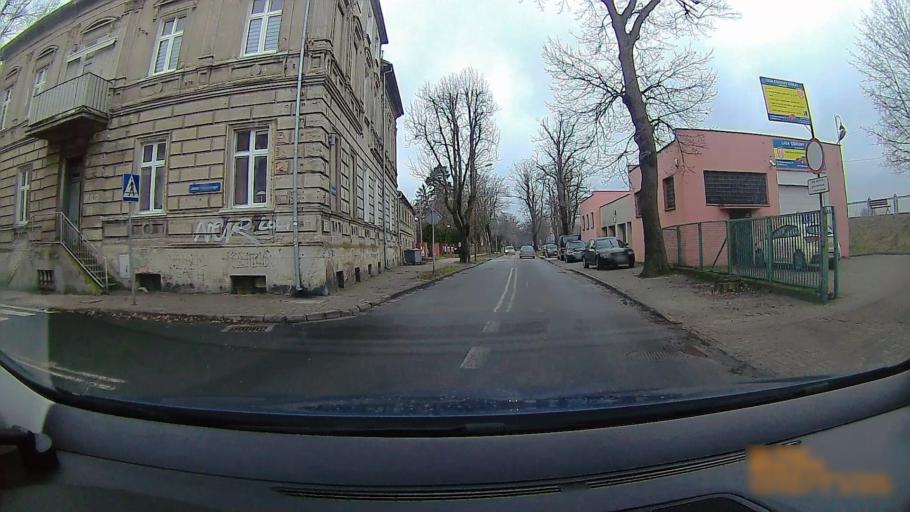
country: PL
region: Greater Poland Voivodeship
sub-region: Konin
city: Konin
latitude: 52.2123
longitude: 18.2509
